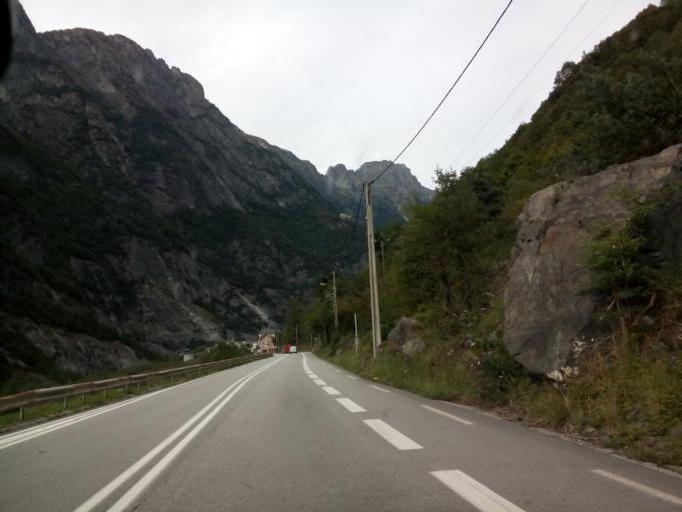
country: FR
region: Rhone-Alpes
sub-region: Departement de l'Isere
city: Livet-et-Gavet
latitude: 45.0864
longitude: 5.9011
